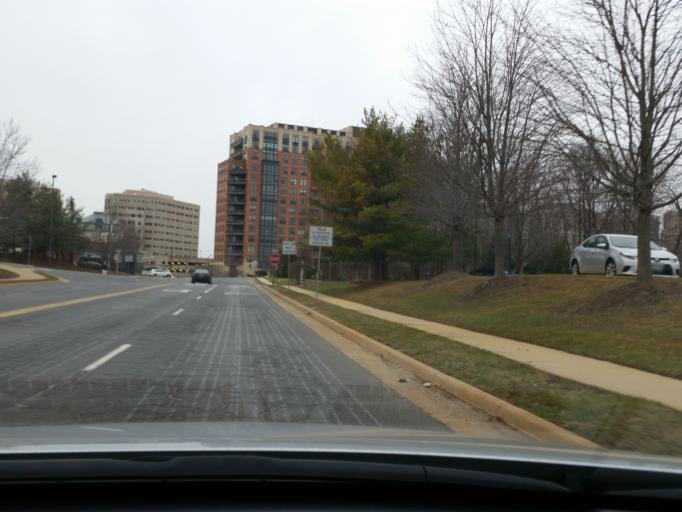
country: US
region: Virginia
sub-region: Fairfax County
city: Reston
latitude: 38.9629
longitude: -77.3564
